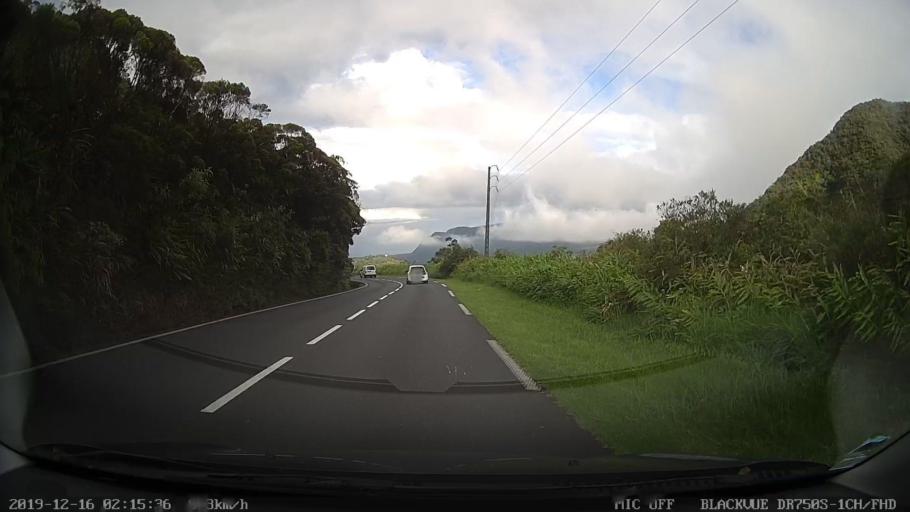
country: RE
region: Reunion
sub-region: Reunion
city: Cilaos
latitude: -21.1573
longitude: 55.5981
